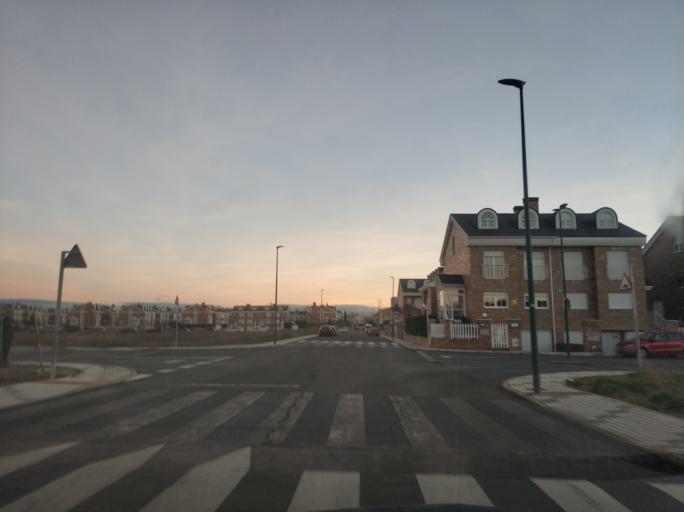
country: ES
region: Castille and Leon
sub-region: Provincia de Salamanca
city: Santa Marta de Tormes
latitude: 40.9553
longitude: -5.6467
